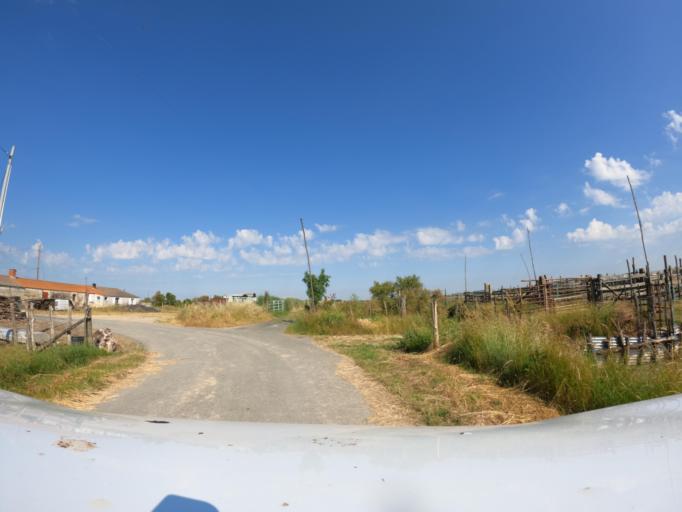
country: FR
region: Pays de la Loire
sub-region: Departement de la Vendee
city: Champagne-les-Marais
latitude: 46.3639
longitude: -1.1167
